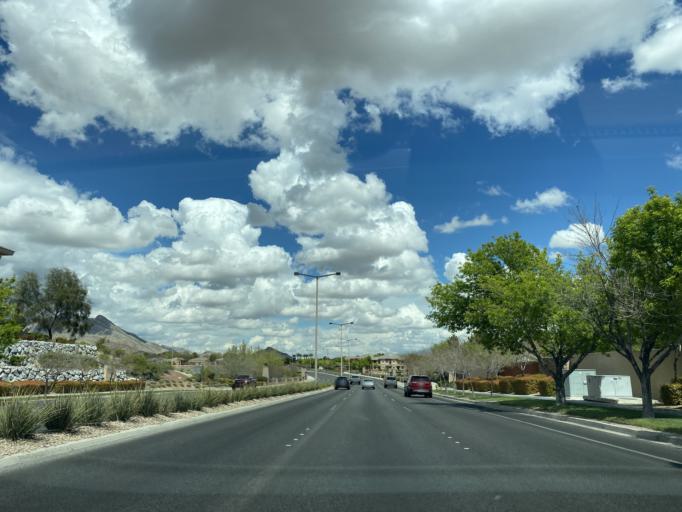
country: US
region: Nevada
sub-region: Clark County
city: Summerlin South
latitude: 36.1611
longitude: -115.3230
